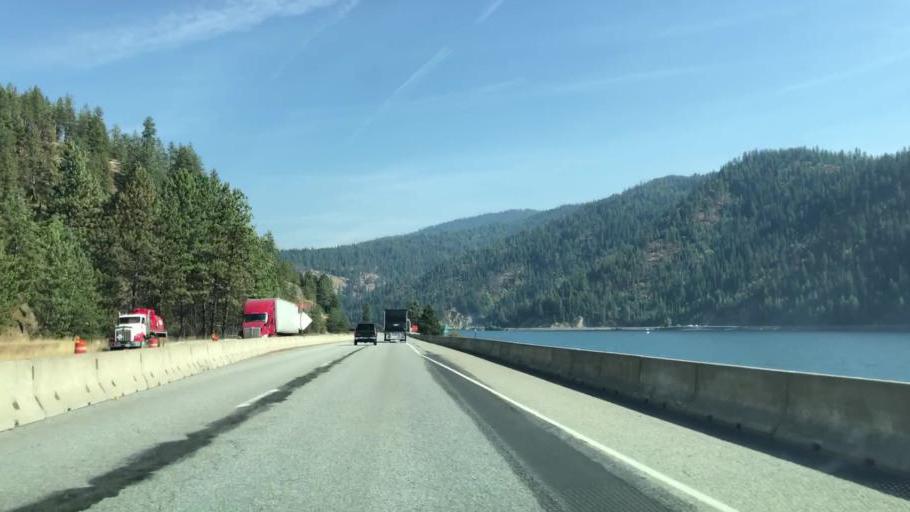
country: US
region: Idaho
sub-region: Kootenai County
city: Coeur d'Alene
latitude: 47.6260
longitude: -116.6727
